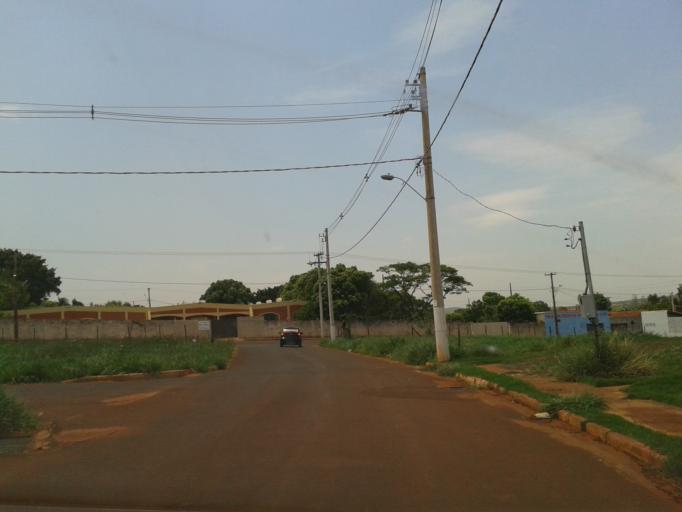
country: BR
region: Minas Gerais
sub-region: Ituiutaba
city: Ituiutaba
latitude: -18.9898
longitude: -49.4372
